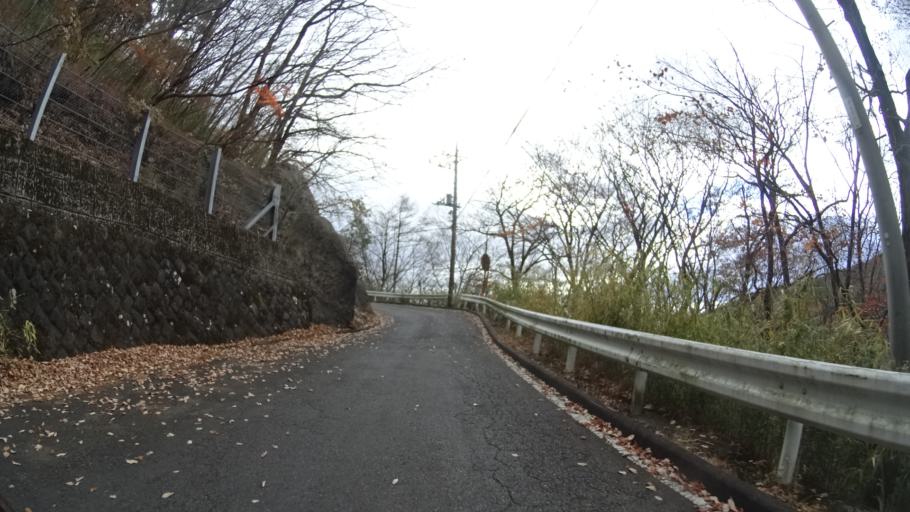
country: JP
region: Gunma
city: Omamacho-omama
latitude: 36.5031
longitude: 139.1814
